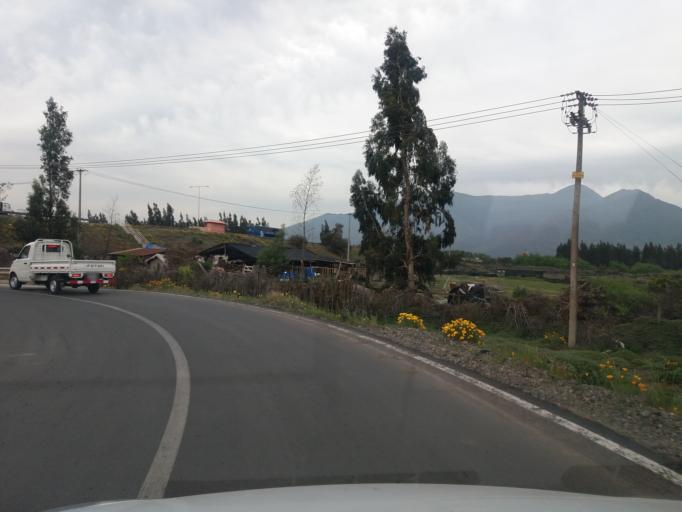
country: CL
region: Valparaiso
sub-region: Provincia de Quillota
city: Hacienda La Calera
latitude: -32.8427
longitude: -71.1095
